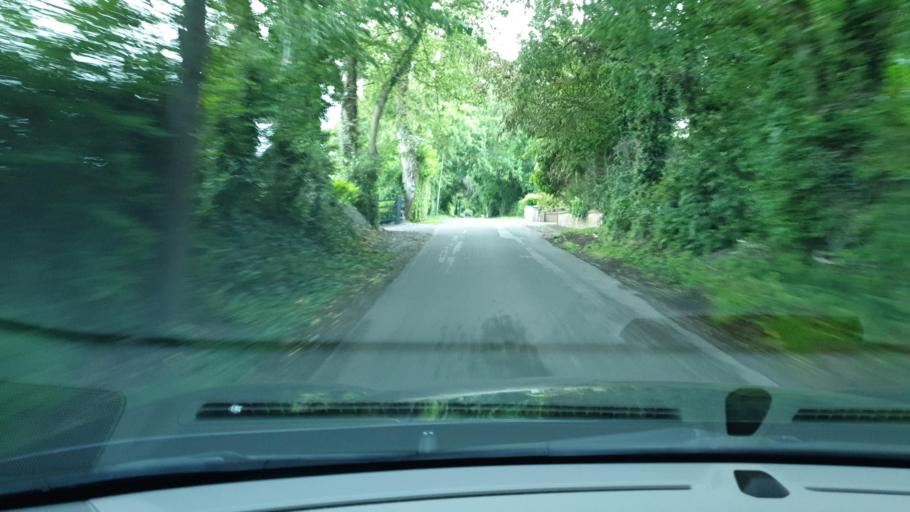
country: IE
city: Kentstown
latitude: 53.5780
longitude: -6.5222
